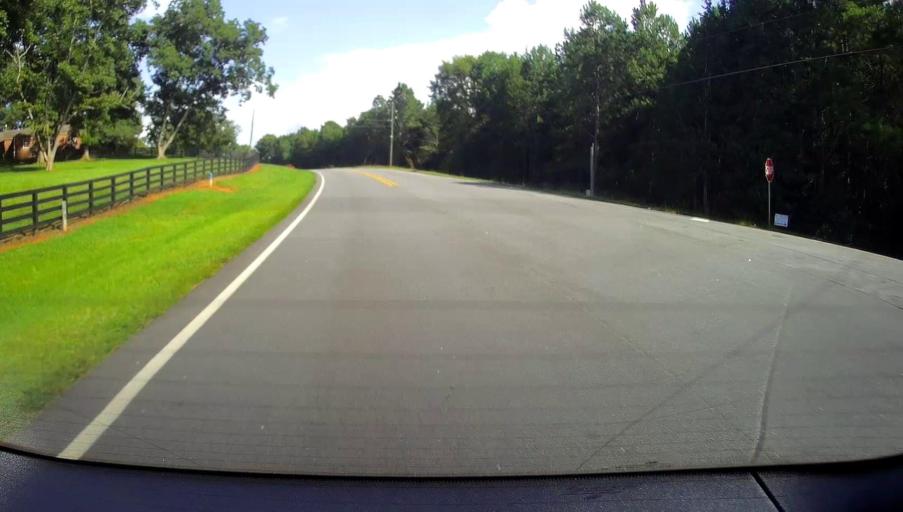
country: US
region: Georgia
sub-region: Upson County
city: Hannahs Mill
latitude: 32.9017
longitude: -84.4214
